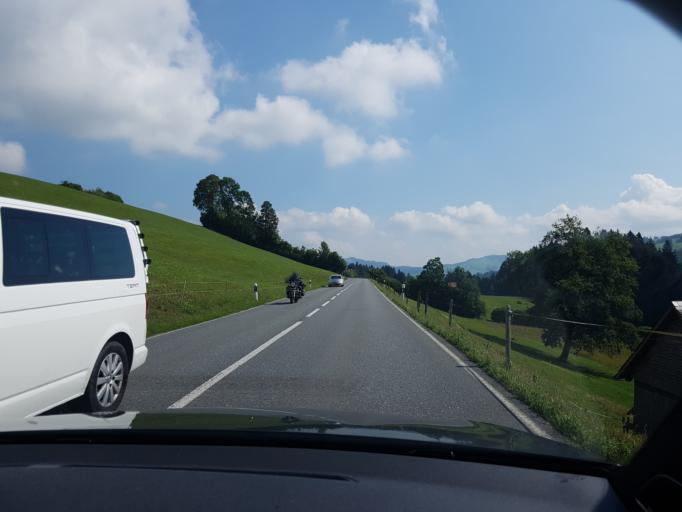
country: CH
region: Saint Gallen
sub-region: Wahlkreis See-Gaster
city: Gommiswald
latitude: 47.2676
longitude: 9.0498
